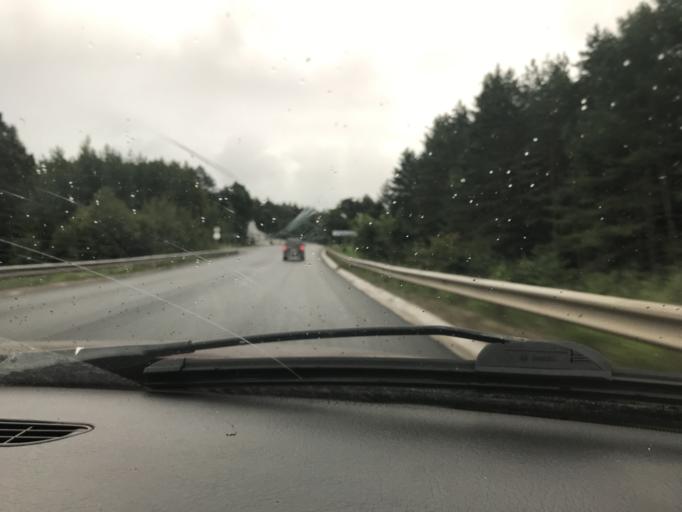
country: RU
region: Kaluga
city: Kurovskoye
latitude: 54.6063
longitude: 36.0450
